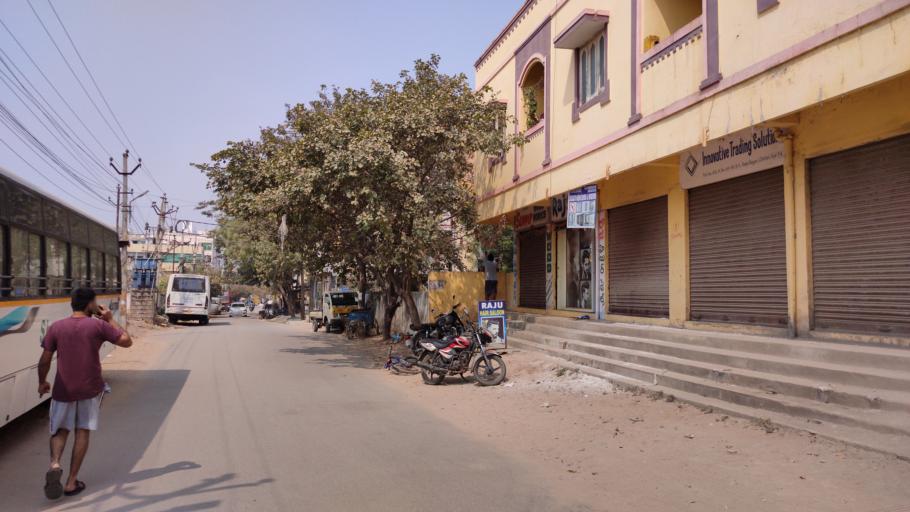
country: IN
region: Telangana
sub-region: Rangareddi
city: Quthbullapur
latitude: 17.4918
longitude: 78.4621
